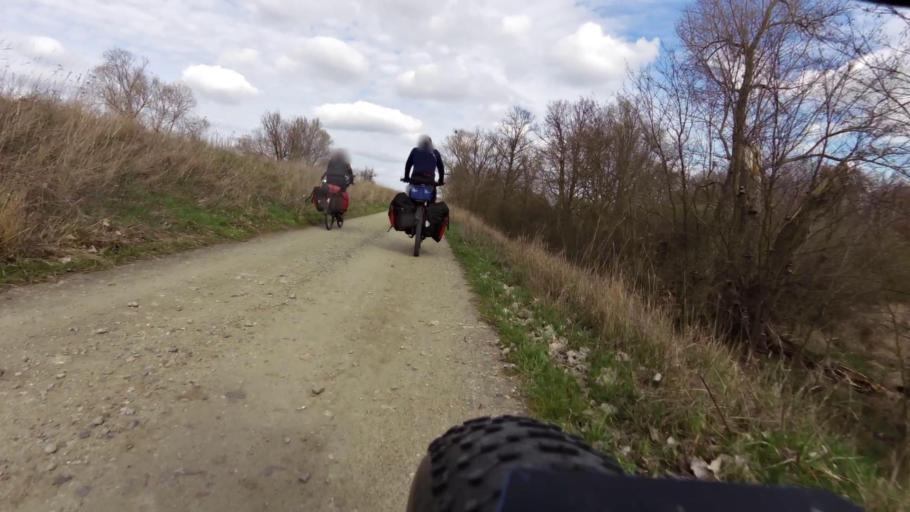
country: DE
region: Brandenburg
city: Lebus
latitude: 52.4354
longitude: 14.5596
